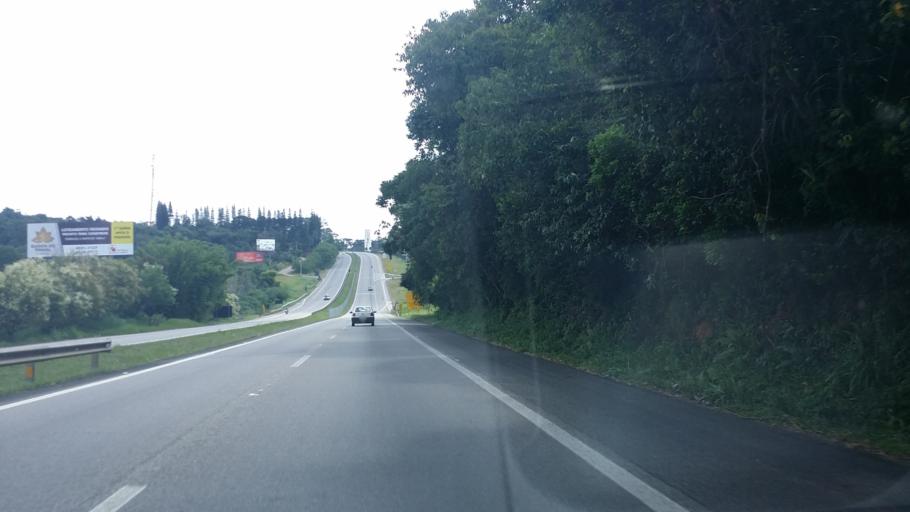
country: BR
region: Sao Paulo
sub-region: Itupeva
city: Itupeva
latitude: -23.1997
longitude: -47.0006
